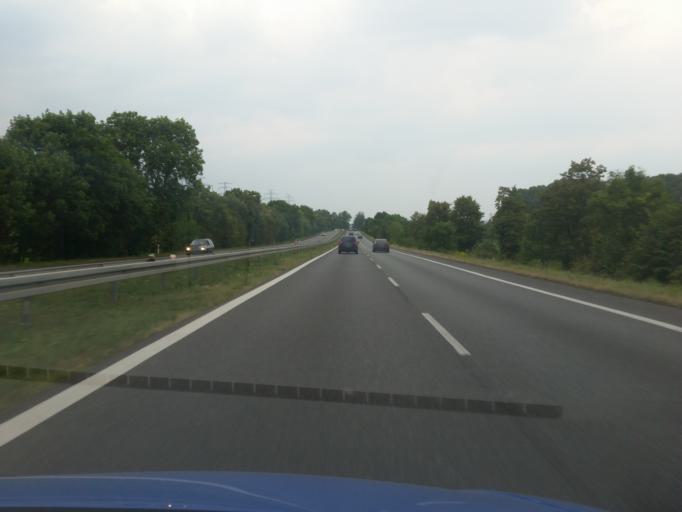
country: PL
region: Silesian Voivodeship
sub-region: Powiat bedzinski
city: Bedzin
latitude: 50.3430
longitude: 19.1103
